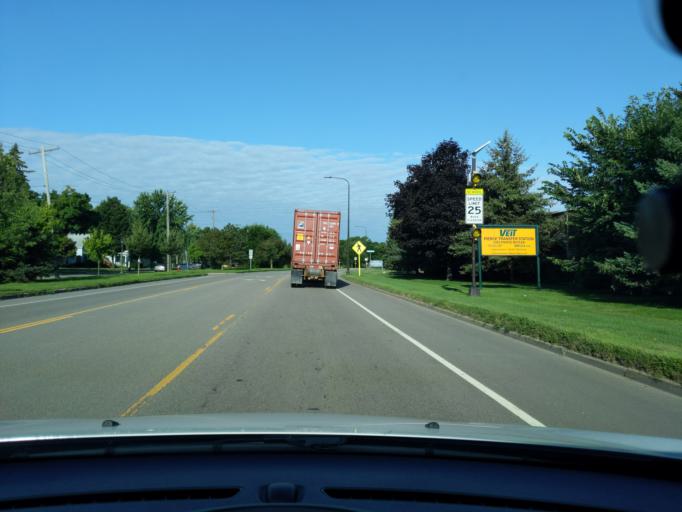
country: US
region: Minnesota
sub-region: Ramsey County
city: Falcon Heights
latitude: 44.9677
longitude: -93.1547
